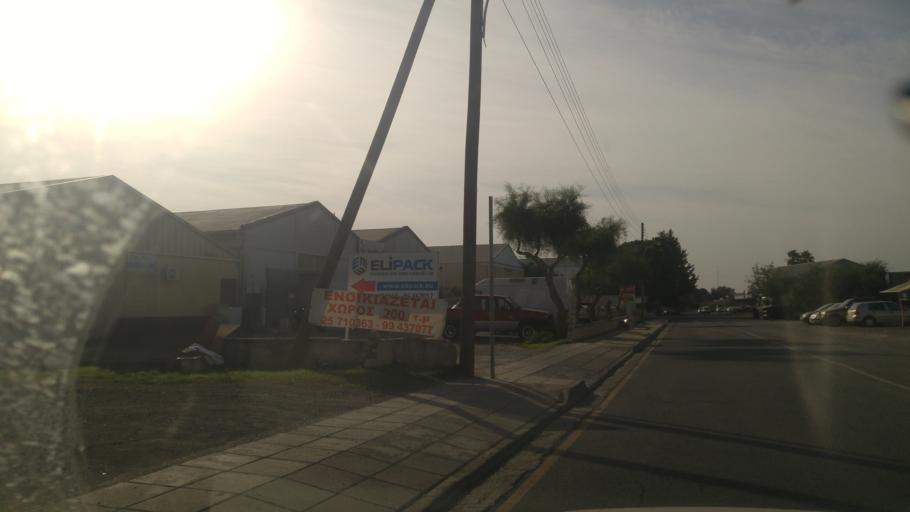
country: CY
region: Limassol
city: Pano Polemidia
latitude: 34.6730
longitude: 32.9936
